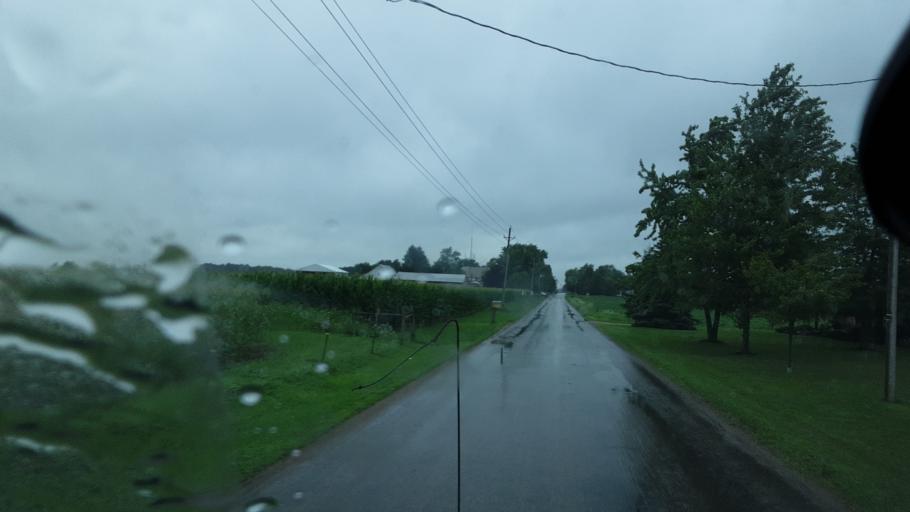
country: US
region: Indiana
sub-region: Adams County
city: Berne
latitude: 40.7128
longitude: -84.8532
